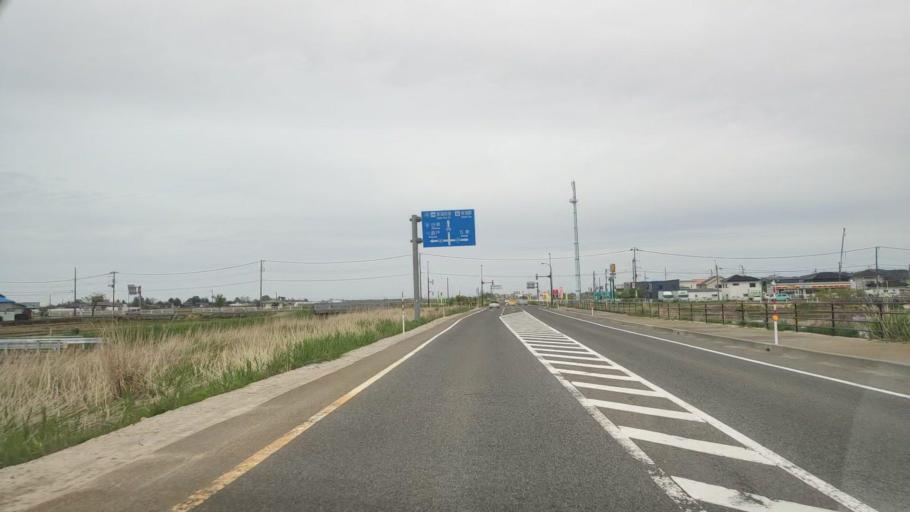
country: JP
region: Niigata
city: Niitsu-honcho
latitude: 37.7498
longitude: 139.0867
